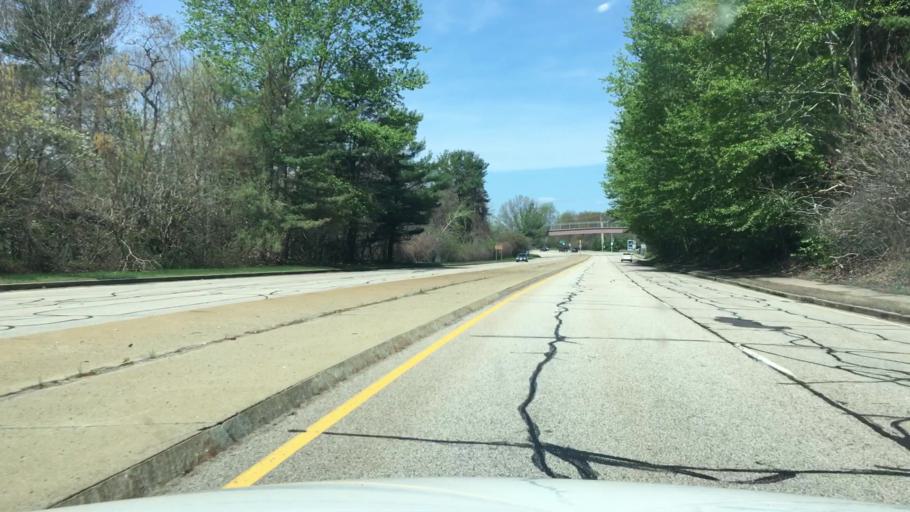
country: US
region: Maine
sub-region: York County
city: South Eliot
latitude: 43.0853
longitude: -70.7818
